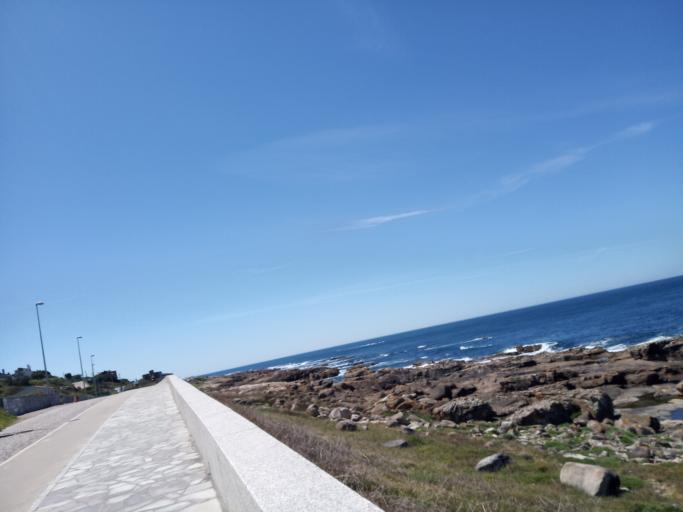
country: ES
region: Galicia
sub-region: Provincia de Pontevedra
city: A Guarda
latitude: 41.8913
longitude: -8.8802
